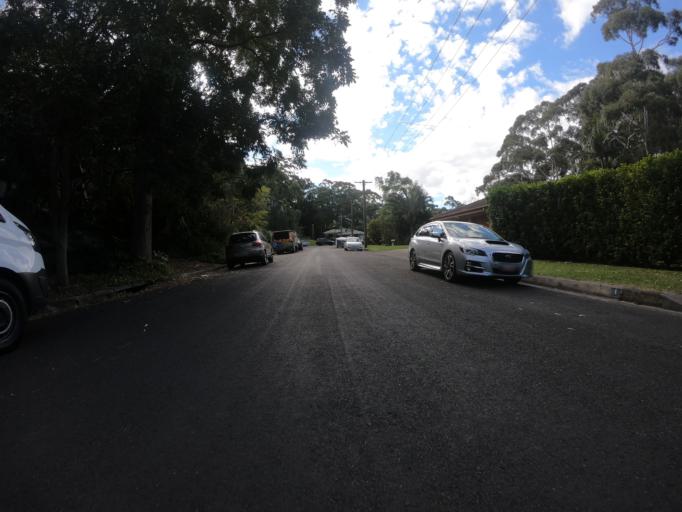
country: AU
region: New South Wales
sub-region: Wollongong
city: Bulli
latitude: -34.3323
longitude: 150.8997
